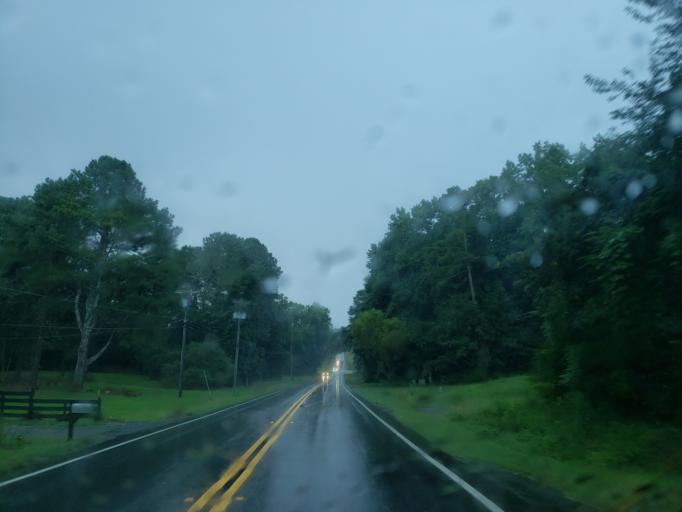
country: US
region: Georgia
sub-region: Cherokee County
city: Canton
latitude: 34.3113
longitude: -84.4620
